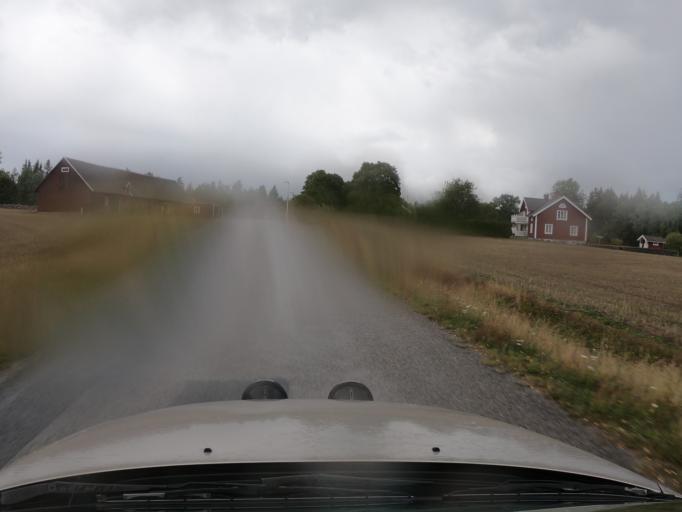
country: SE
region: Joenkoeping
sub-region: Vetlanda Kommun
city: Landsbro
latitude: 57.2617
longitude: 14.8336
